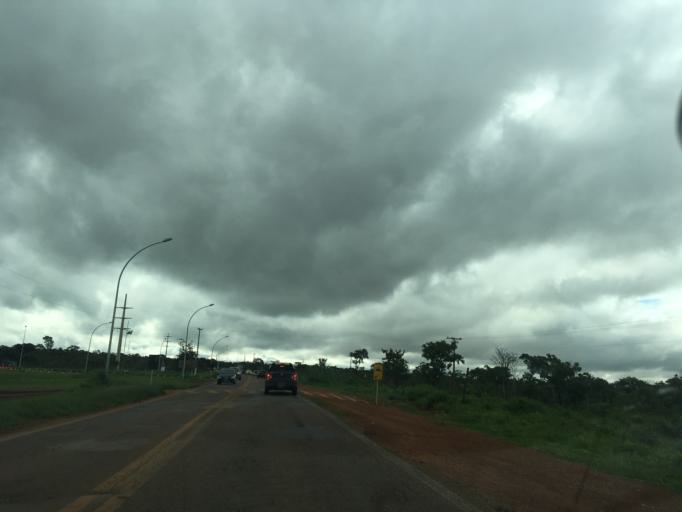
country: BR
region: Federal District
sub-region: Brasilia
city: Brasilia
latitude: -15.9745
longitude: -47.9771
